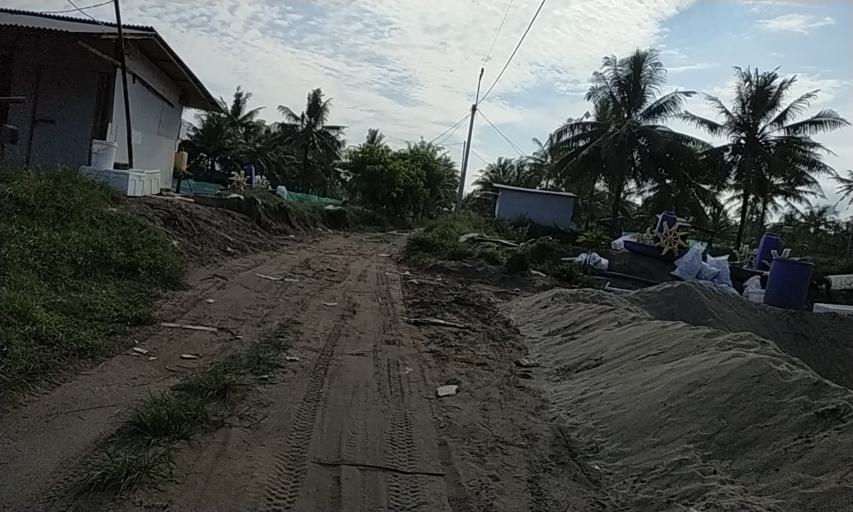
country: ID
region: Central Java
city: Gombong
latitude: -7.7620
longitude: 109.5145
